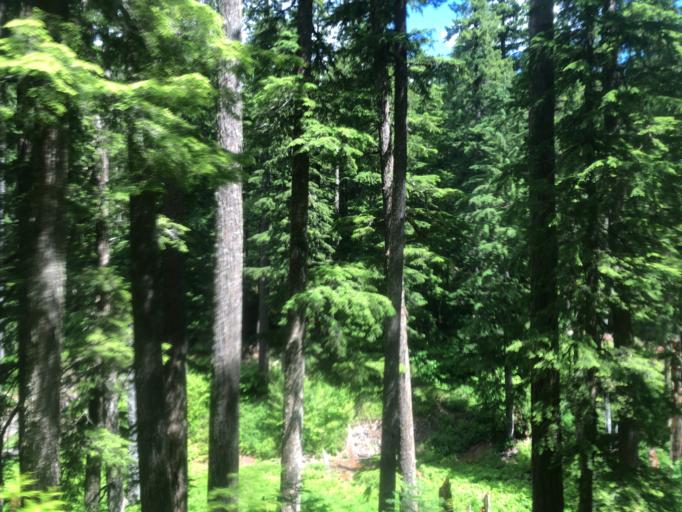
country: US
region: Oregon
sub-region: Clackamas County
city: Mount Hood Village
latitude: 45.4626
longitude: -121.8498
